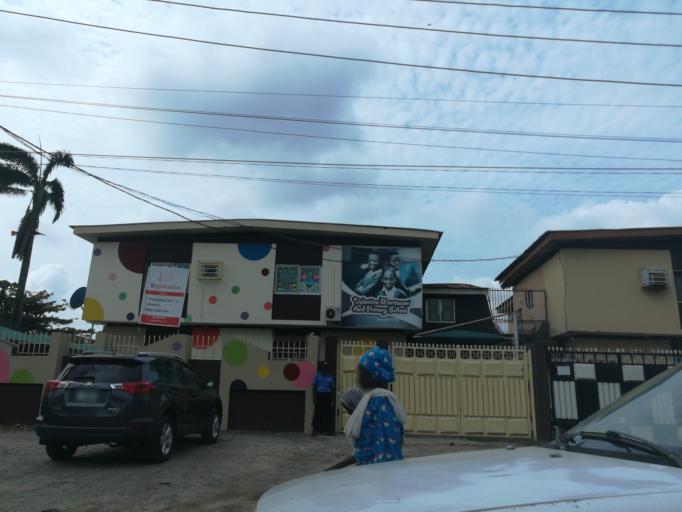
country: NG
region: Lagos
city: Somolu
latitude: 6.5472
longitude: 3.3845
